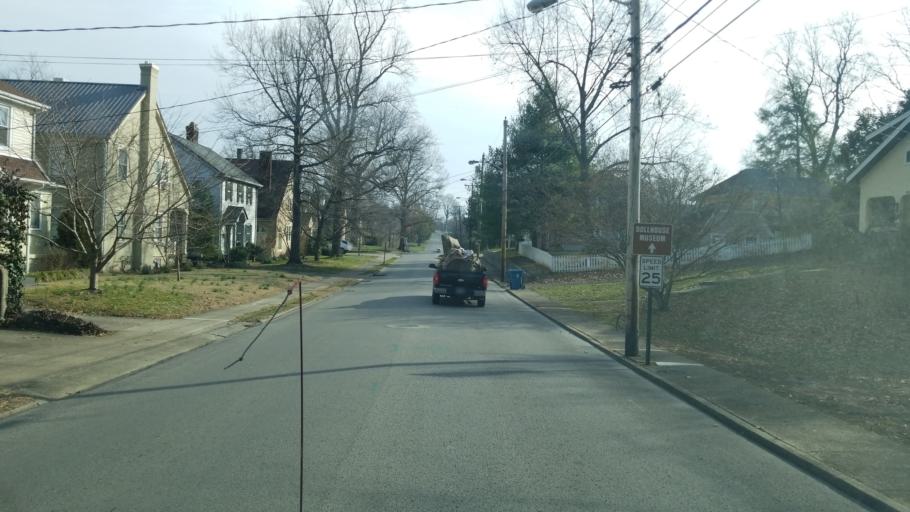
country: US
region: Kentucky
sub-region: Boyle County
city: Danville
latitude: 37.6497
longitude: -84.7815
